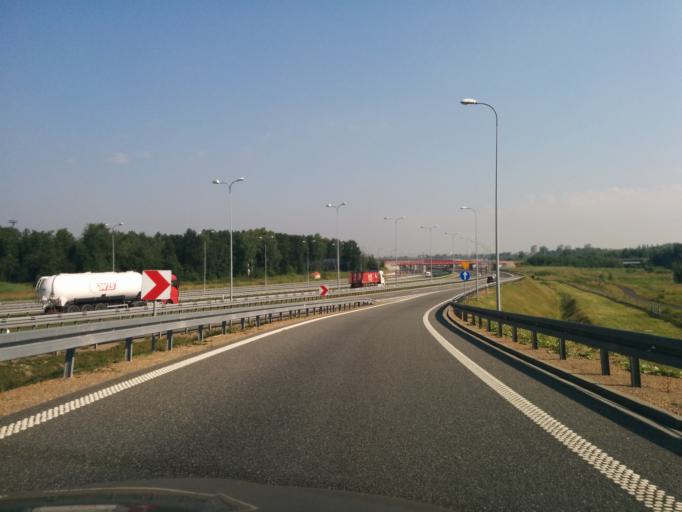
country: PL
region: Silesian Voivodeship
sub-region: Powiat gliwicki
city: Przyszowice
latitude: 50.2698
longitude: 18.7296
